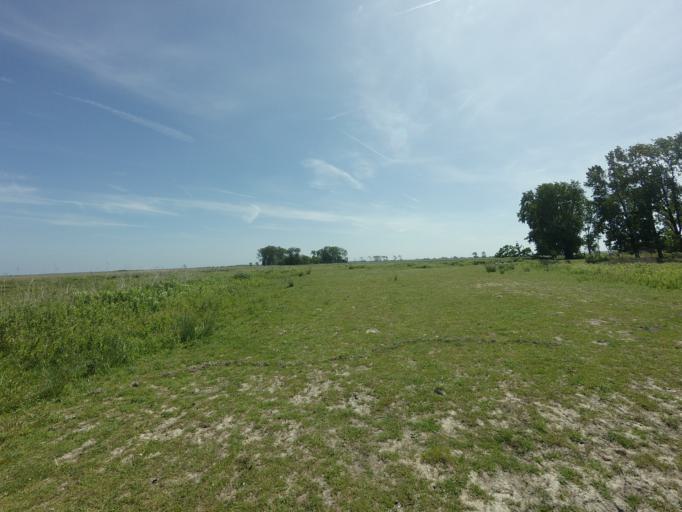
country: NL
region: South Holland
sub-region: Gemeente Spijkenisse
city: Spijkenisse
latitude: 51.7437
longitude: 4.3033
